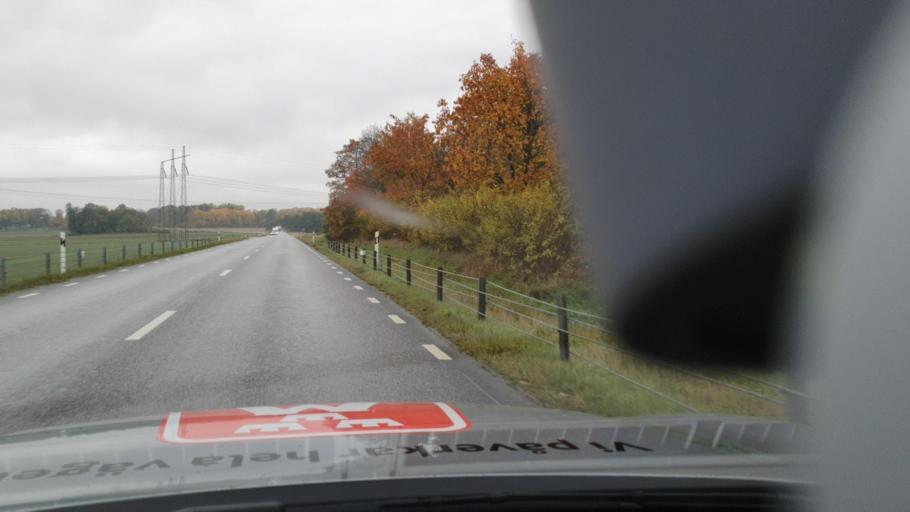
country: SE
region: Stockholm
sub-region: Sigtuna Kommun
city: Marsta
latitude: 59.7531
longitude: 17.9991
